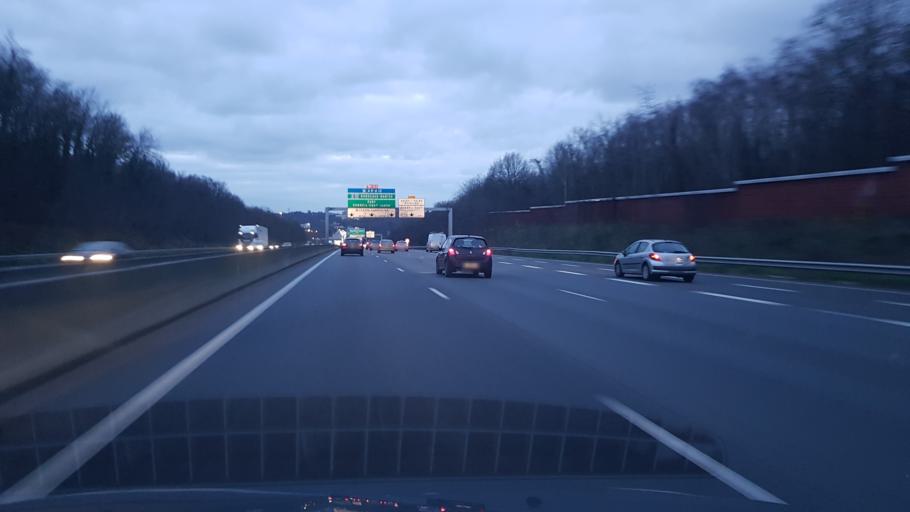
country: FR
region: Ile-de-France
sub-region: Departement de l'Essonne
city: Etiolles
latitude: 48.6311
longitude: 2.4854
